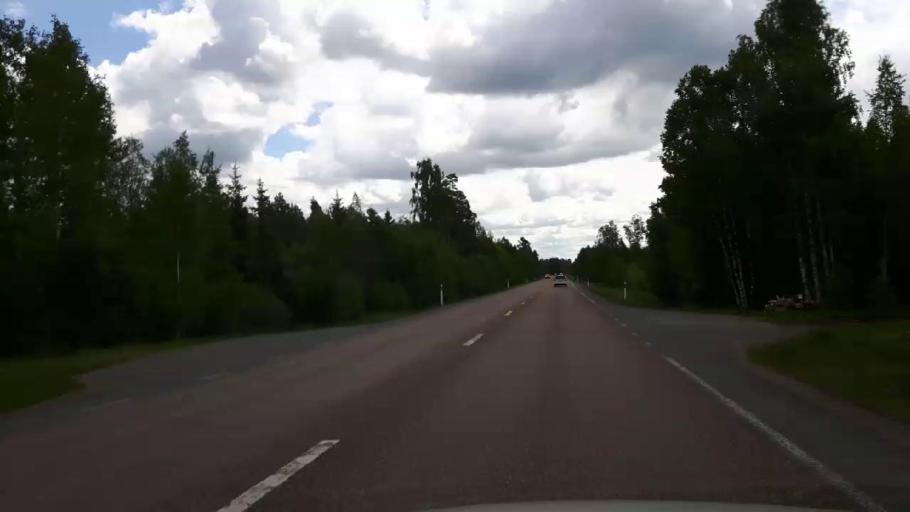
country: SE
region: Dalarna
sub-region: Saters Kommun
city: Saeter
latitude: 60.4946
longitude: 15.7592
